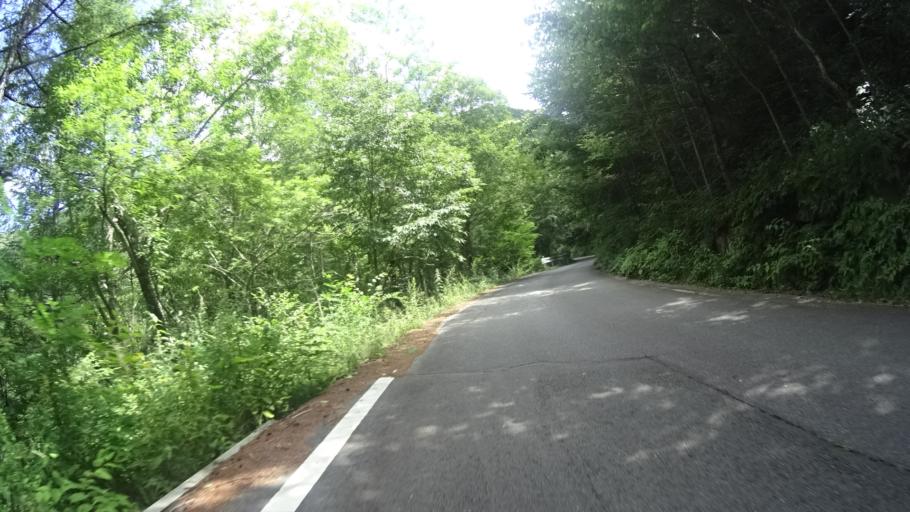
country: JP
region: Yamanashi
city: Enzan
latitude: 35.8335
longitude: 138.6392
